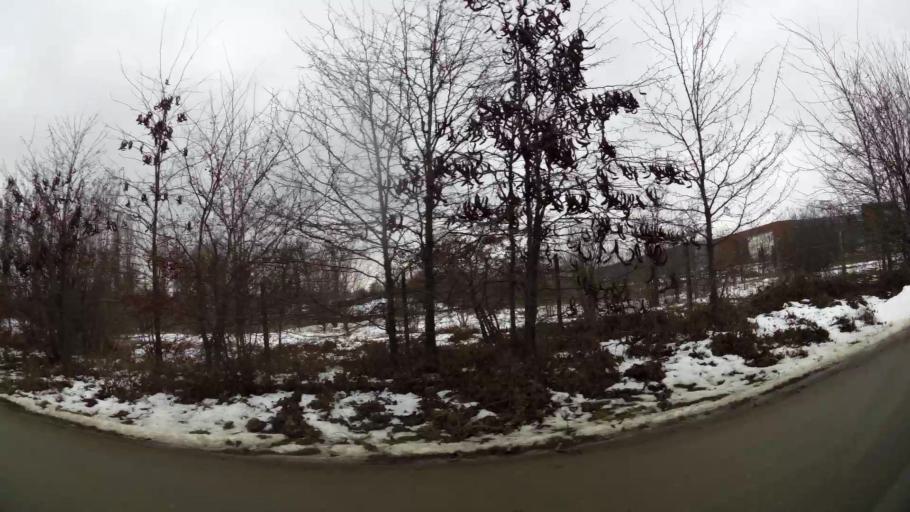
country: RO
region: Ilfov
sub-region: Comuna Chitila
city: Chitila
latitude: 44.5015
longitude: 26.0072
